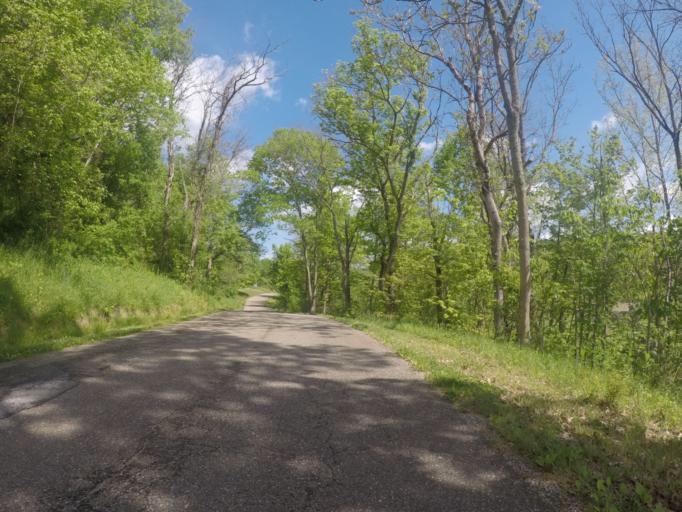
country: US
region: West Virginia
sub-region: Cabell County
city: Huntington
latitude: 38.5193
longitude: -82.4401
